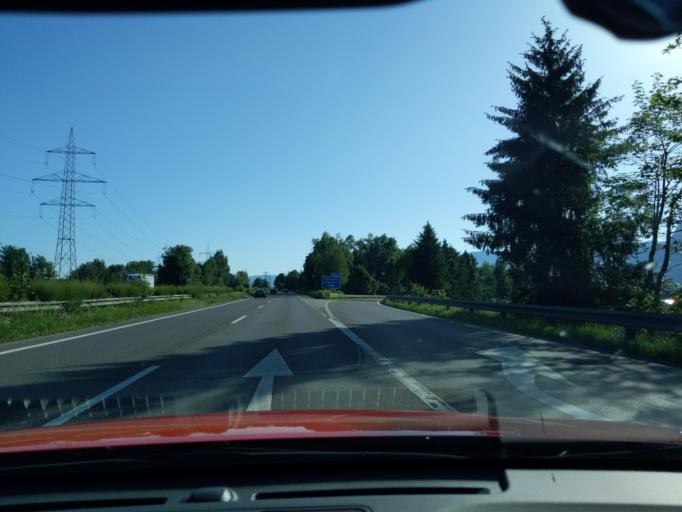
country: CH
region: Saint Gallen
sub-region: Wahlkreis Rheintal
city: Diepoldsau
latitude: 47.3724
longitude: 9.6662
